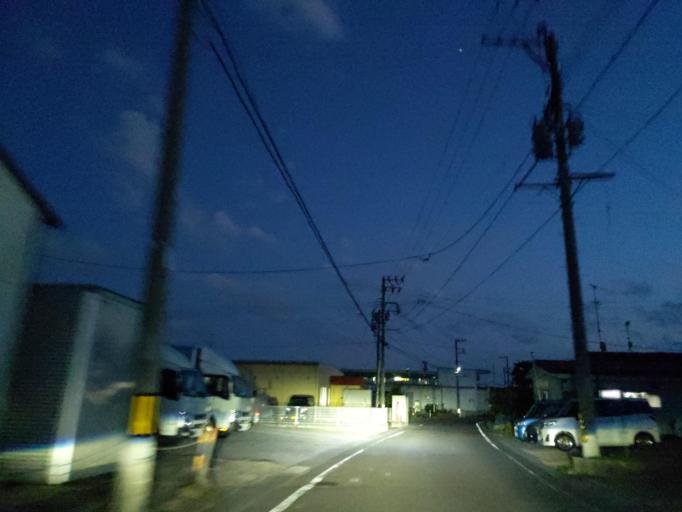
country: JP
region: Fukushima
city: Koriyama
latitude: 37.4305
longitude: 140.3348
